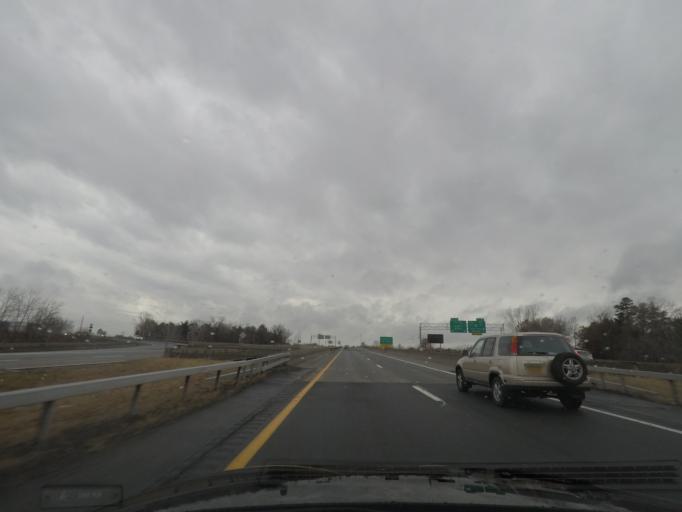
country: US
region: New York
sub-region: Albany County
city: McKownville
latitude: 42.6986
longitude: -73.8366
